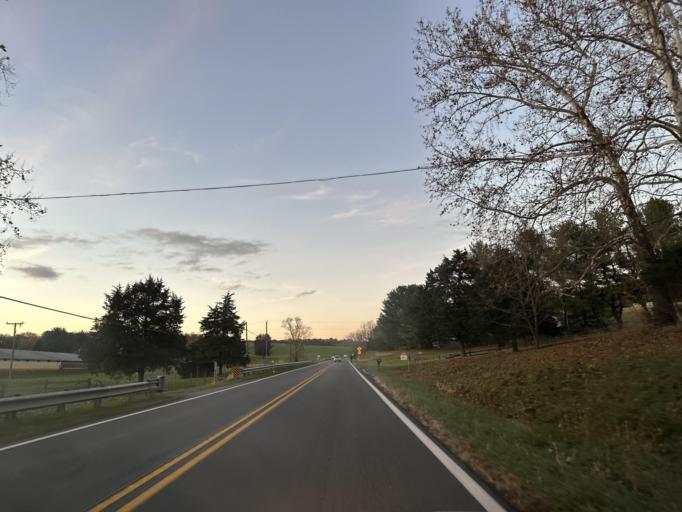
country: US
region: Virginia
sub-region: Rockingham County
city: Bridgewater
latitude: 38.4230
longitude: -79.0147
